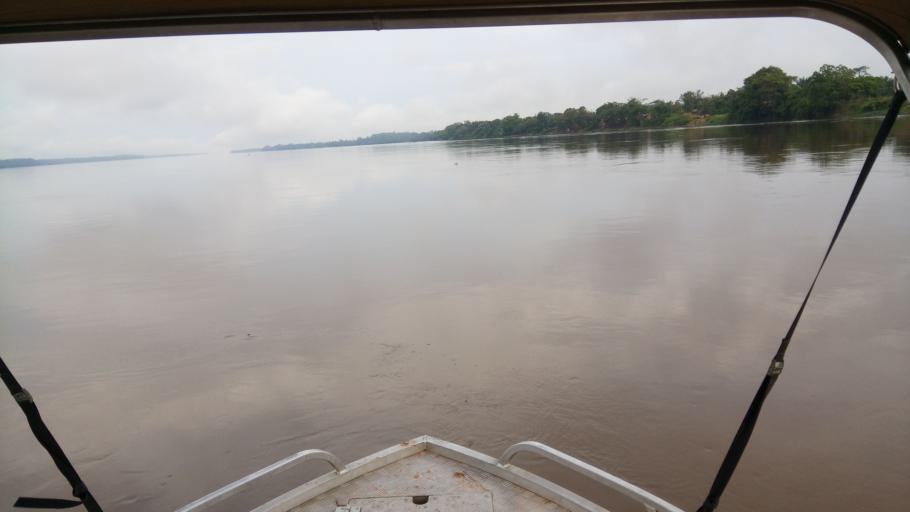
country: CD
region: Eastern Province
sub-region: Sous-Region de la Tshopo
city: Yangambi
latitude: 0.6085
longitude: 24.7242
